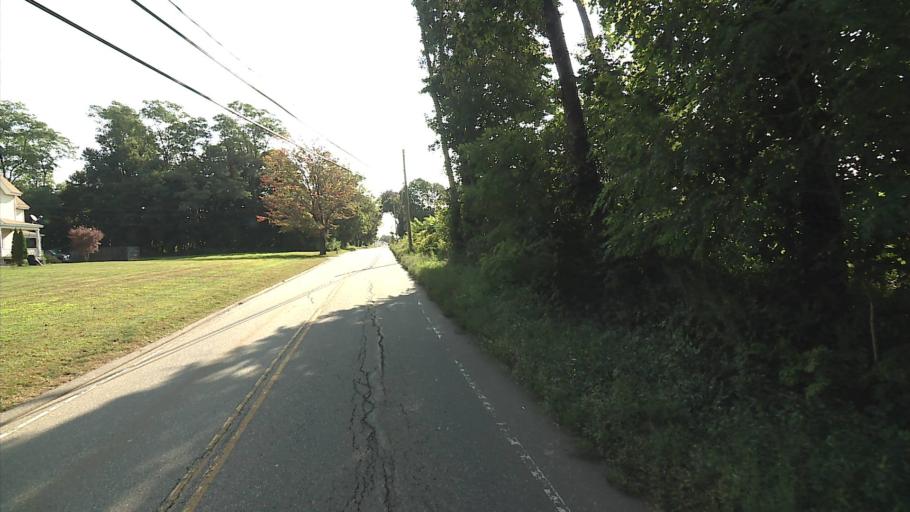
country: US
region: Connecticut
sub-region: Windham County
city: South Windham
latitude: 41.6133
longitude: -72.1843
